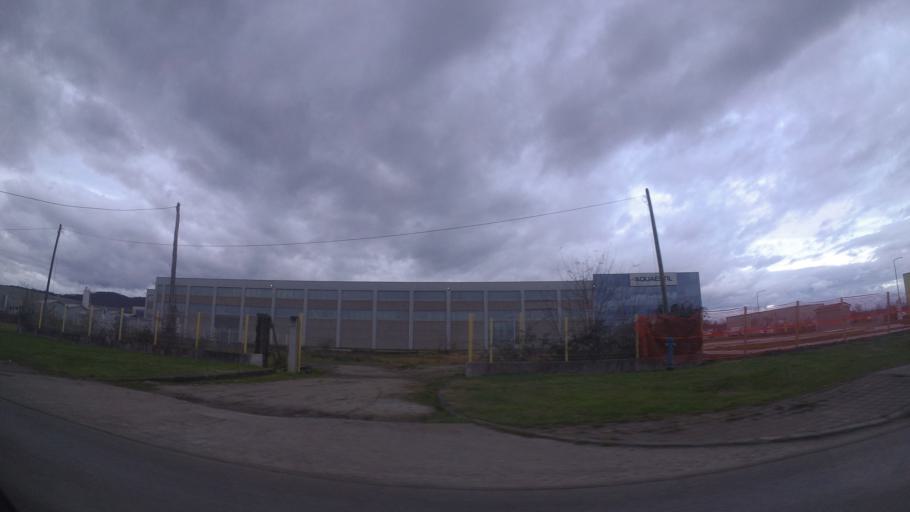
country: HR
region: Karlovacka
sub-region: Grad Karlovac
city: Karlovac
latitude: 45.4542
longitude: 15.5618
